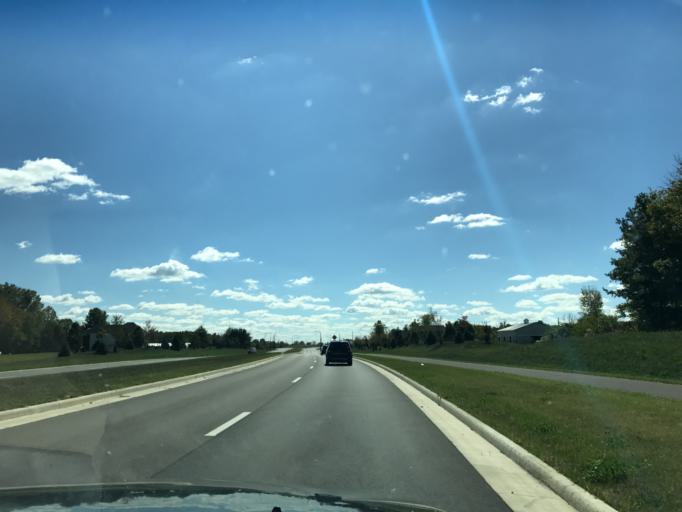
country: US
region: Ohio
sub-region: Delaware County
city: Delaware
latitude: 40.2481
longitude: -83.0930
